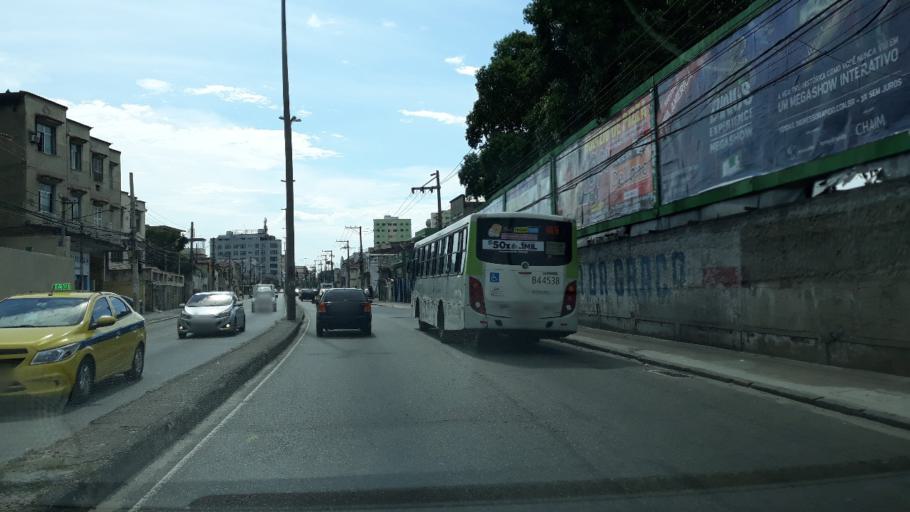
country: BR
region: Rio de Janeiro
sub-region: Duque De Caxias
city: Duque de Caxias
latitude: -22.8851
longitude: -43.3111
